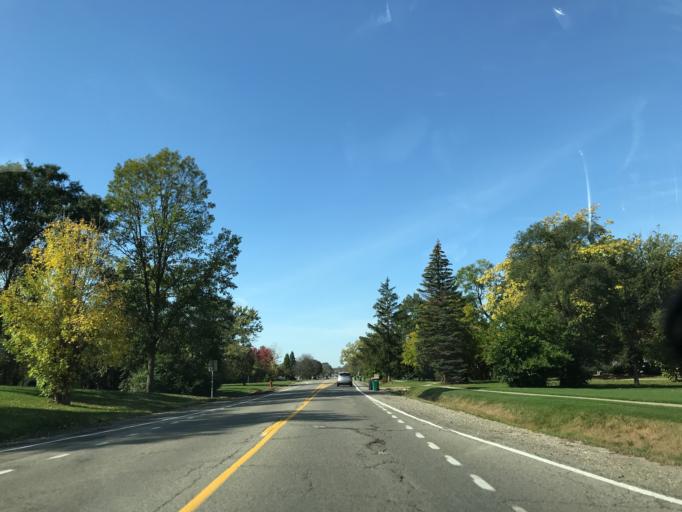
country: US
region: Michigan
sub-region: Oakland County
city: Farmington
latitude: 42.4704
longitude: -83.3486
